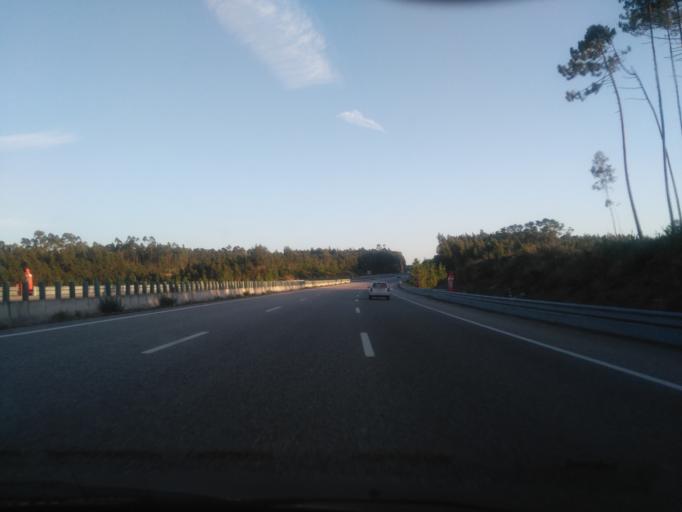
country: PT
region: Leiria
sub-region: Pombal
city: Lourical
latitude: 40.0025
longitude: -8.7990
